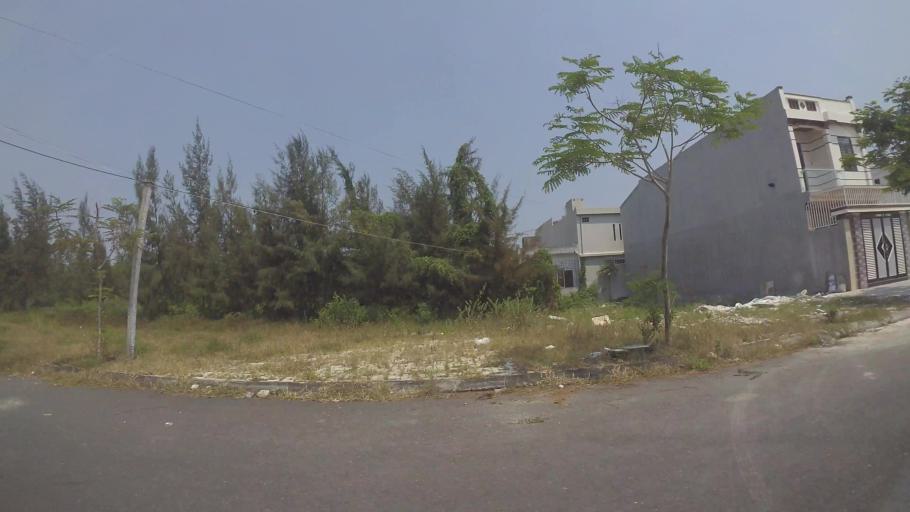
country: VN
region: Da Nang
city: Ngu Hanh Son
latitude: 15.9869
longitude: 108.2674
